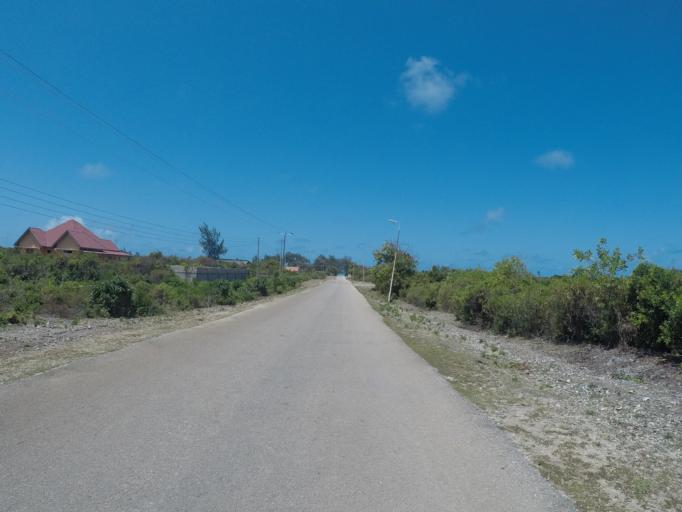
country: TZ
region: Zanzibar Central/South
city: Nganane
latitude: -6.4103
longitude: 39.5696
